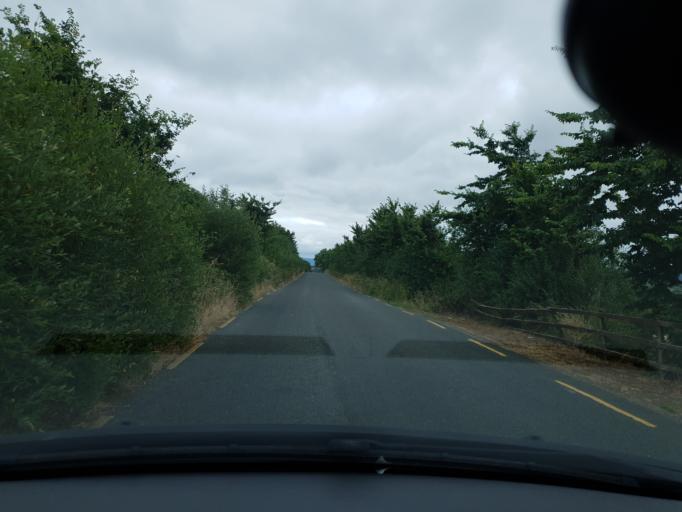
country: IE
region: Munster
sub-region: Ciarrai
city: Cill Airne
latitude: 52.1378
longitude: -9.5845
